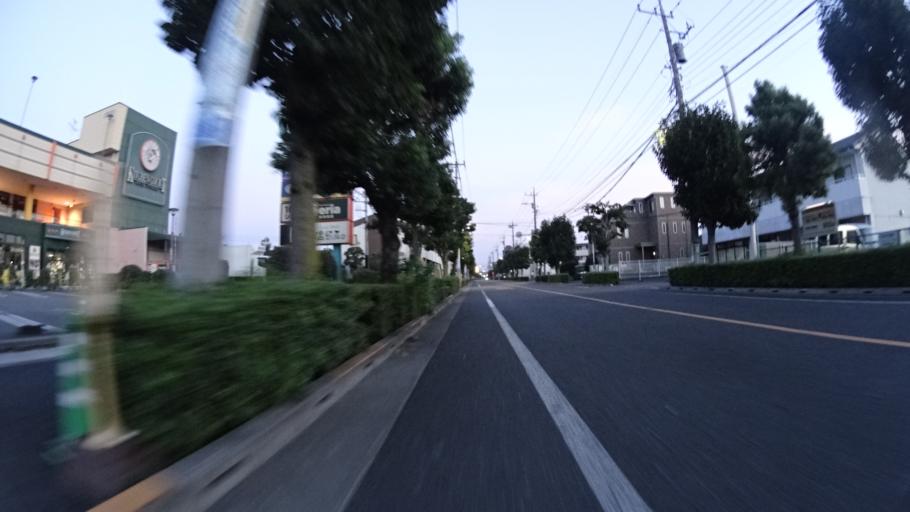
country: JP
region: Tokyo
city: Chofugaoka
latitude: 35.6540
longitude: 139.5309
